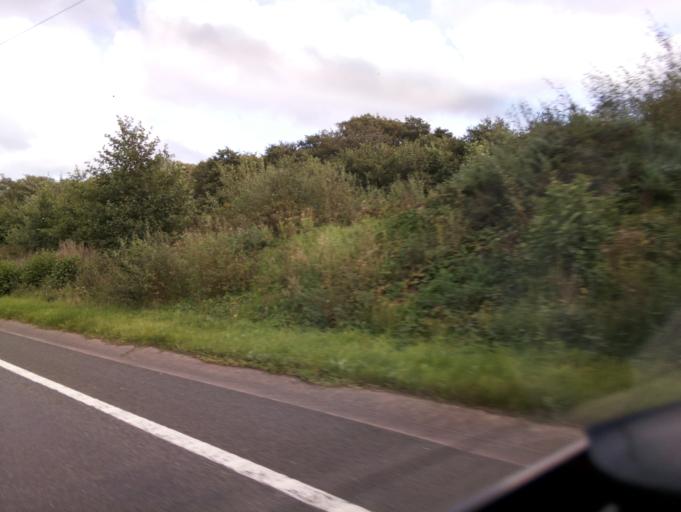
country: GB
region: Wales
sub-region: Rhondda Cynon Taf
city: Llantwit Fardre
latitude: 51.5549
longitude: -3.3231
